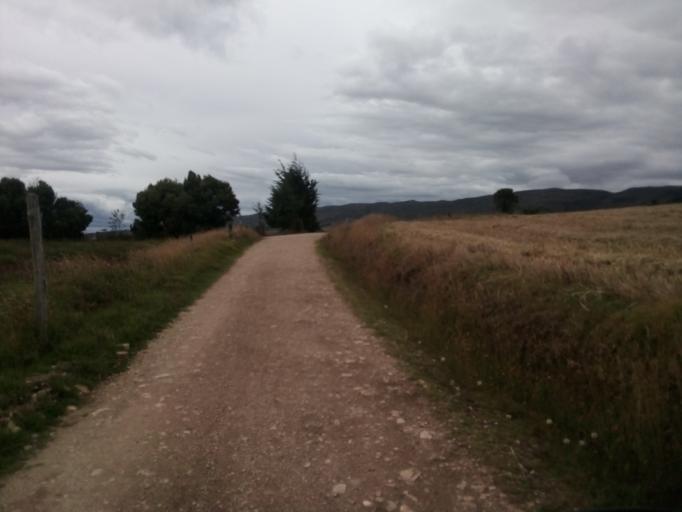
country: CO
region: Boyaca
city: Toca
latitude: 5.5917
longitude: -73.1345
